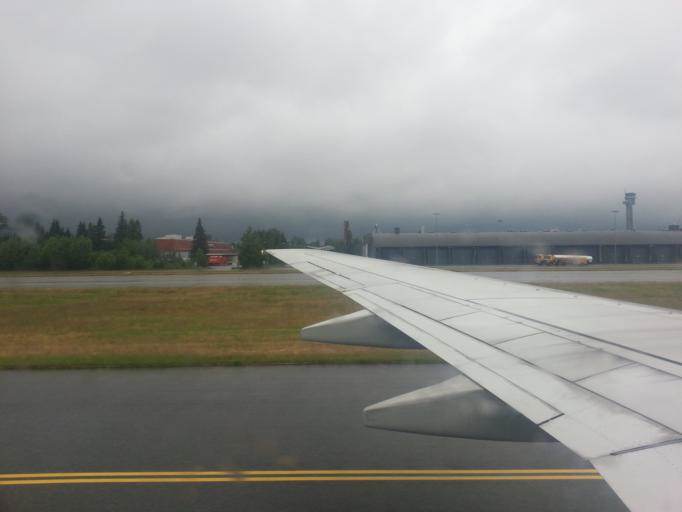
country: NO
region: Akershus
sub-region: Ullensaker
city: Jessheim
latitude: 60.1870
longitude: 11.1100
